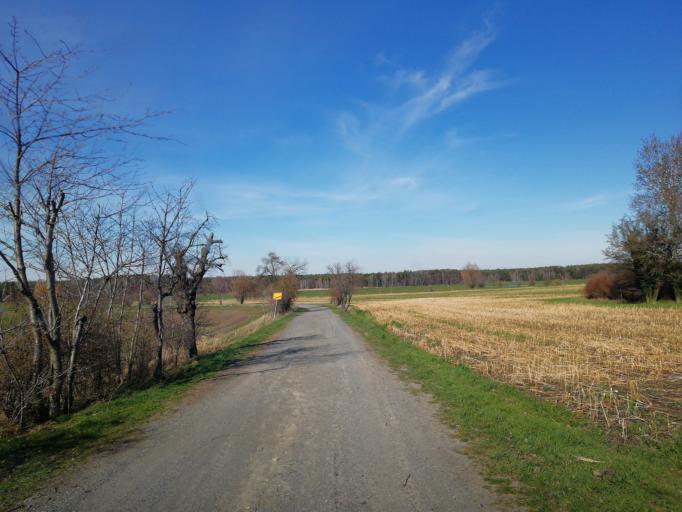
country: DE
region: Brandenburg
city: Ruckersdorf
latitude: 51.5563
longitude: 13.5925
